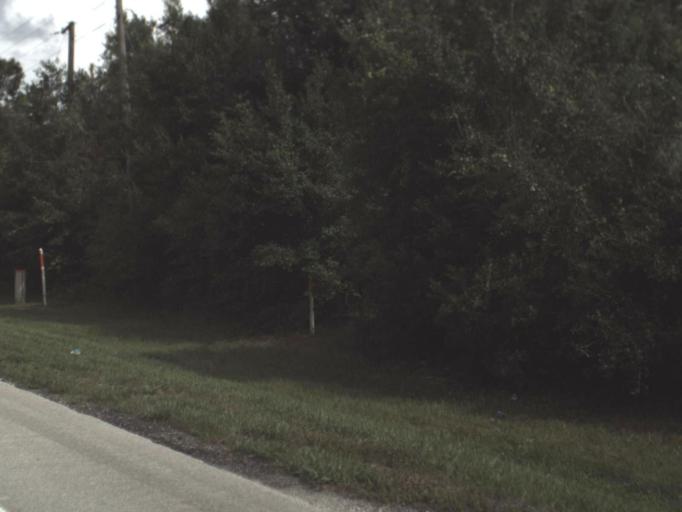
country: US
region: Florida
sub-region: DeSoto County
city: Nocatee
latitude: 27.2010
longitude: -81.9723
